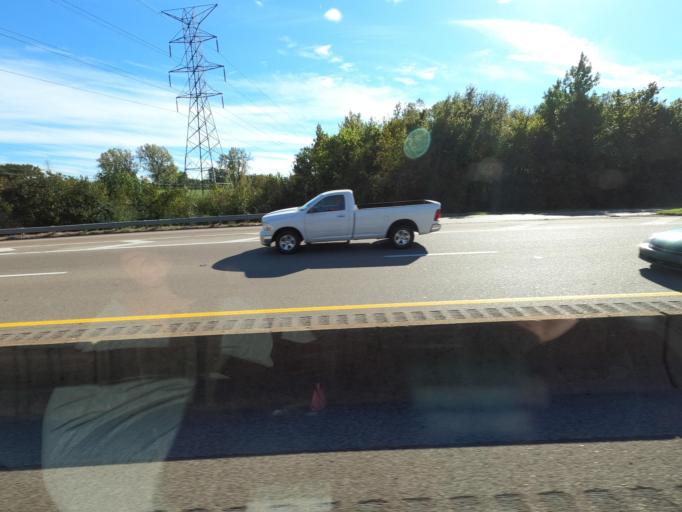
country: US
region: Tennessee
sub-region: Shelby County
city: New South Memphis
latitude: 35.0784
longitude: -90.0543
